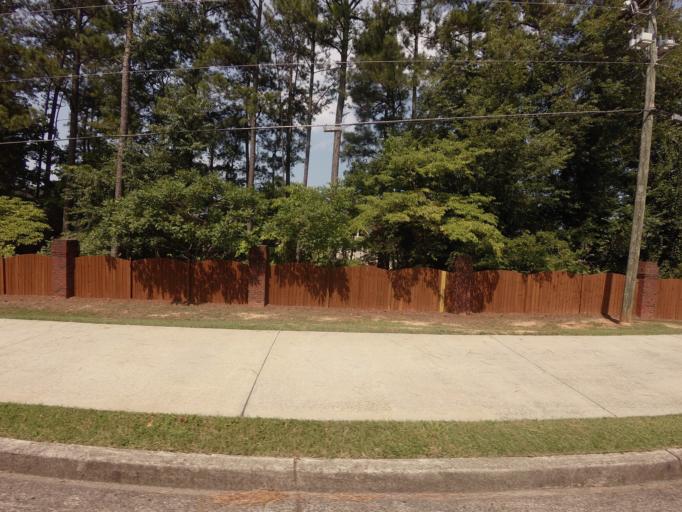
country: US
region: Georgia
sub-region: Fulton County
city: Johns Creek
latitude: 34.0098
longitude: -84.2633
